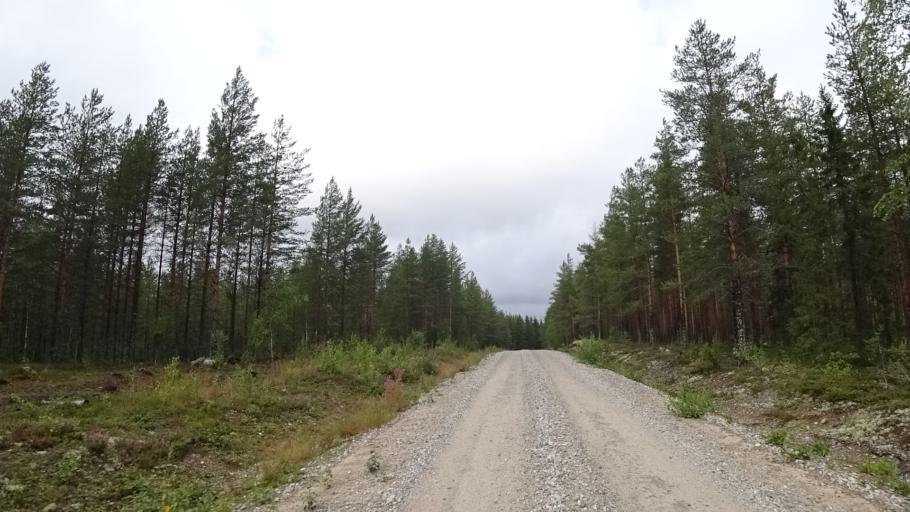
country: FI
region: North Karelia
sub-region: Pielisen Karjala
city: Lieksa
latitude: 63.4737
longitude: 30.2678
